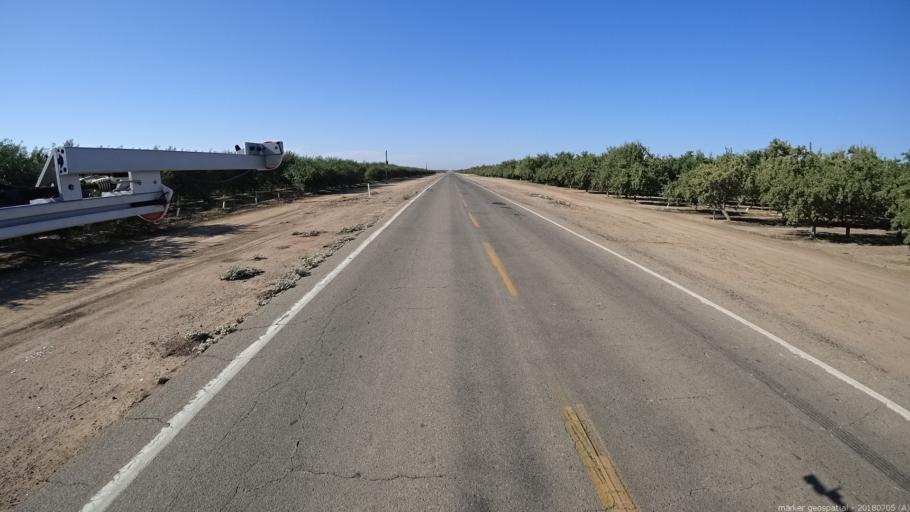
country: US
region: California
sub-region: Madera County
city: Madera Acres
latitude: 37.0939
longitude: -120.0746
